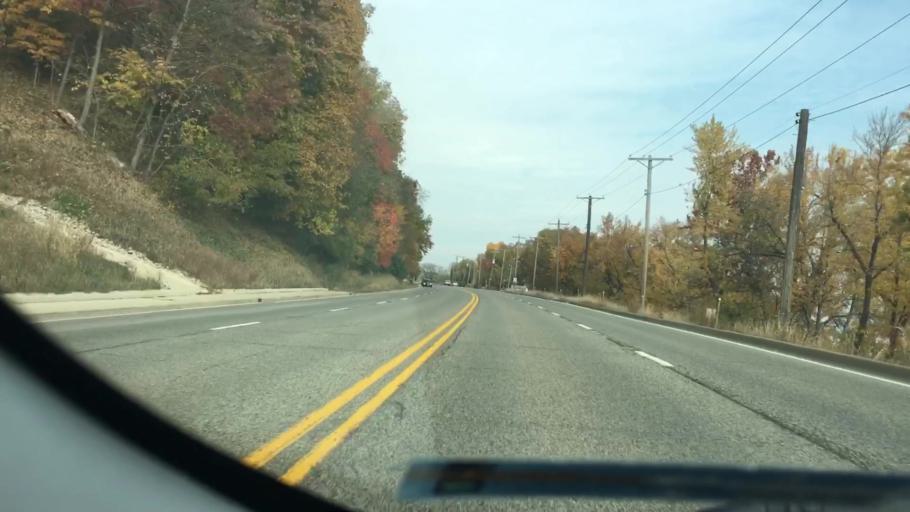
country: US
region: Illinois
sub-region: Peoria County
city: Peoria Heights
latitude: 40.7361
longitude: -89.5519
